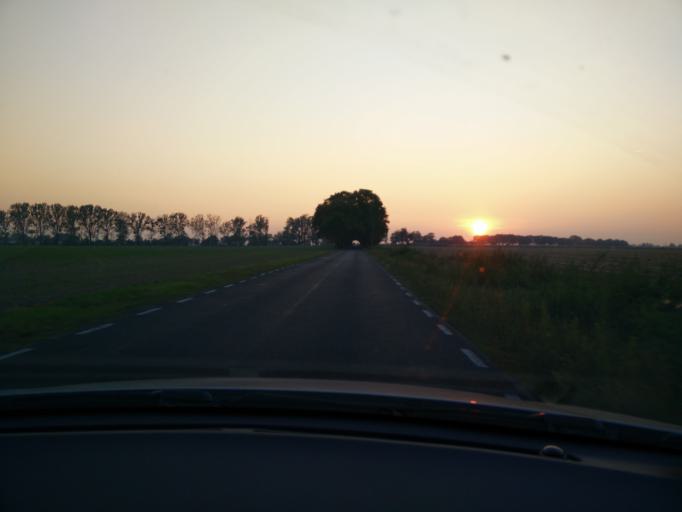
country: PL
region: Greater Poland Voivodeship
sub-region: Powiat sredzki
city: Dominowo
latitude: 52.2112
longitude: 17.3554
